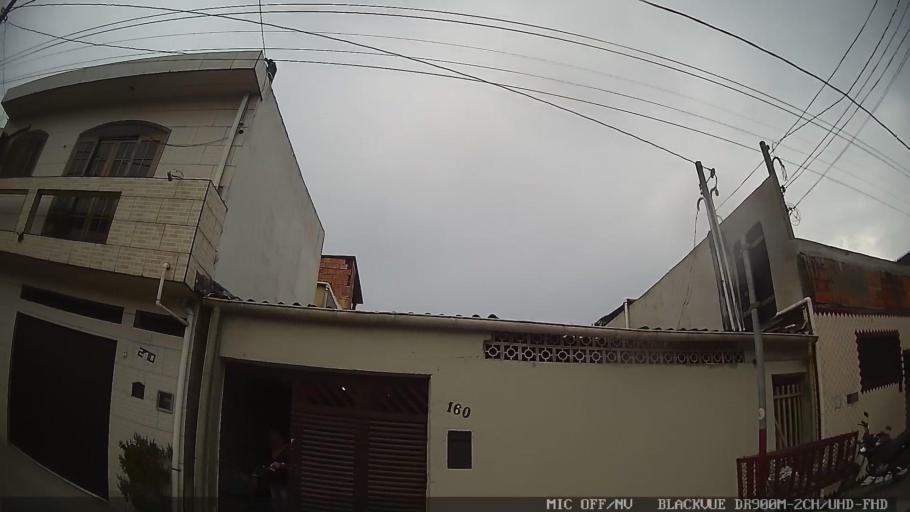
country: BR
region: Sao Paulo
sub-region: Guaruja
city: Guaruja
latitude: -23.9766
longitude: -46.2280
